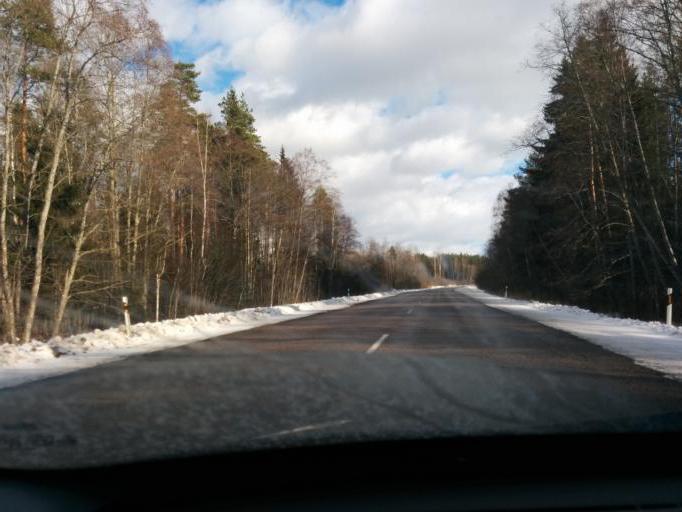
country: LV
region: Gulbenes Rajons
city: Gulbene
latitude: 57.2291
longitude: 26.5220
